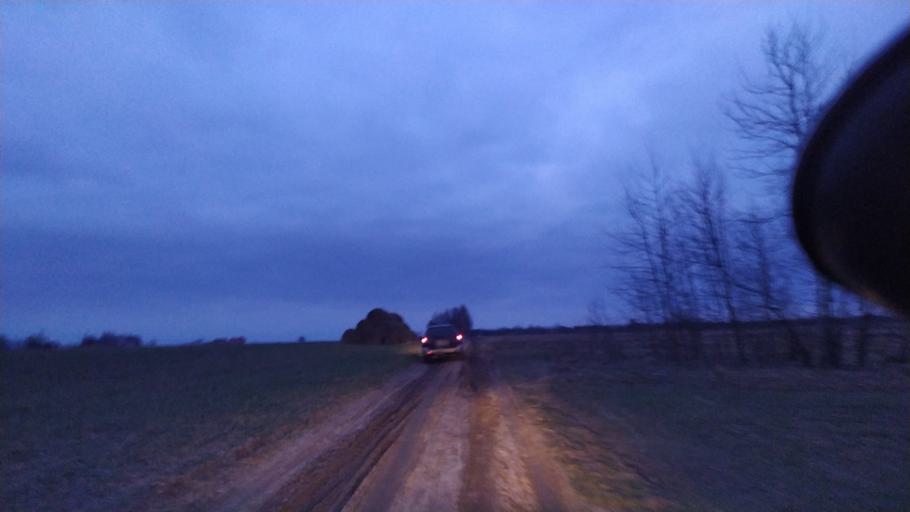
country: PL
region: Lublin Voivodeship
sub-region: Powiat lubartowski
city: Kamionka
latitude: 51.3932
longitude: 22.4296
